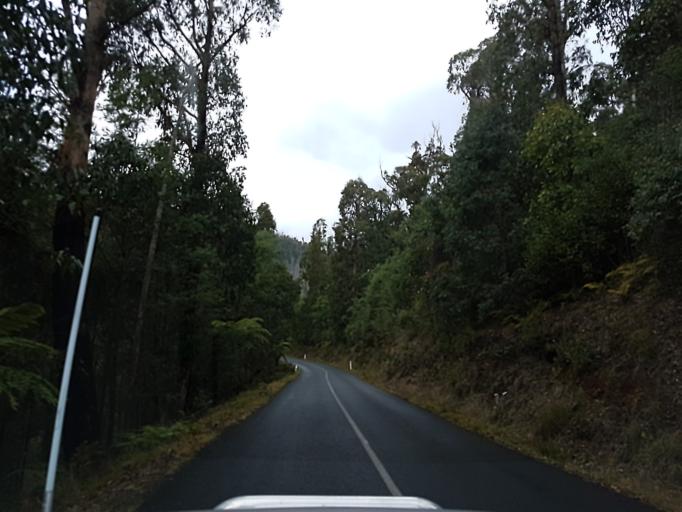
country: AU
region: Victoria
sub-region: Yarra Ranges
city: Millgrove
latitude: -37.5226
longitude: 145.7697
